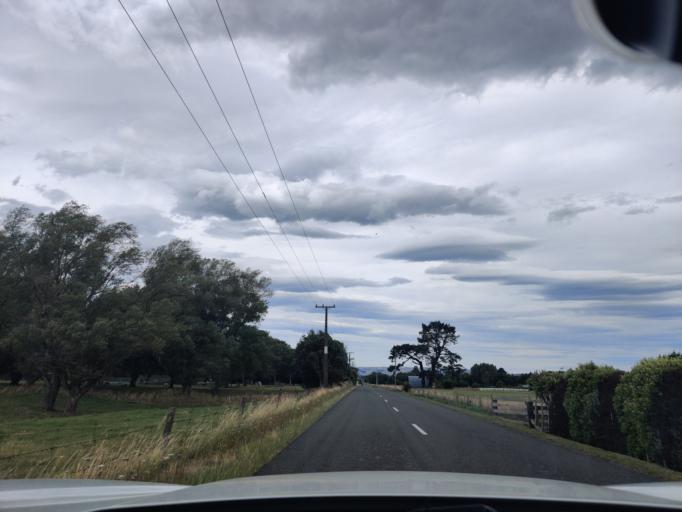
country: NZ
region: Wellington
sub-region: Masterton District
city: Masterton
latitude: -41.0234
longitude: 175.4734
